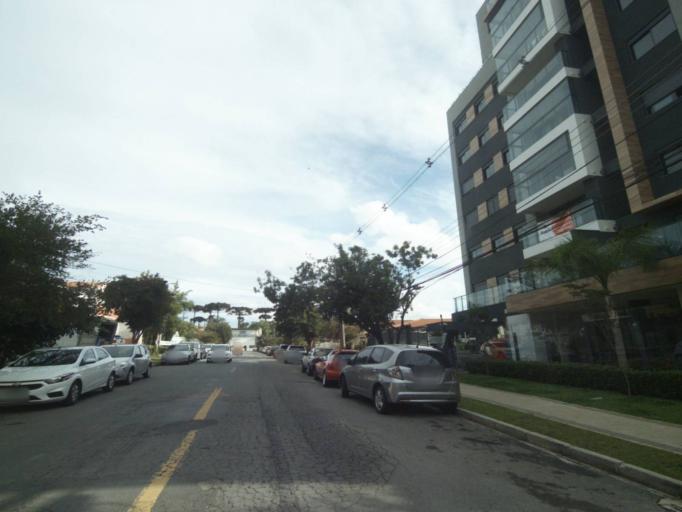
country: BR
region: Parana
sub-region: Curitiba
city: Curitiba
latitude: -25.4372
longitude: -49.3068
